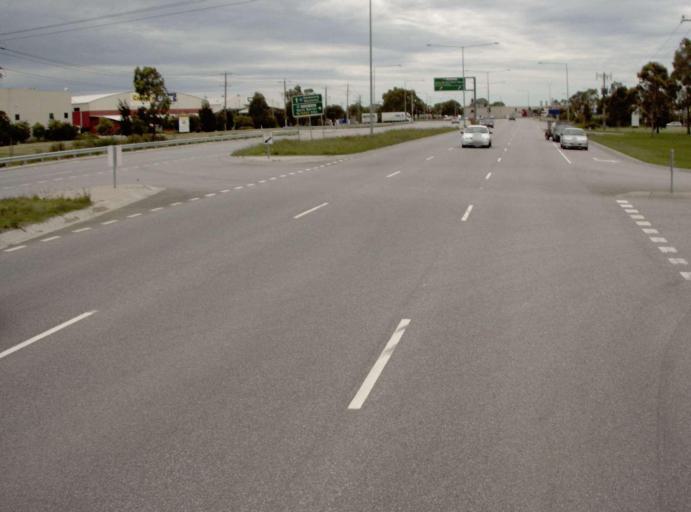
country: AU
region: Victoria
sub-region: Casey
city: Hampton Park
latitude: -38.0295
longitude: 145.2442
